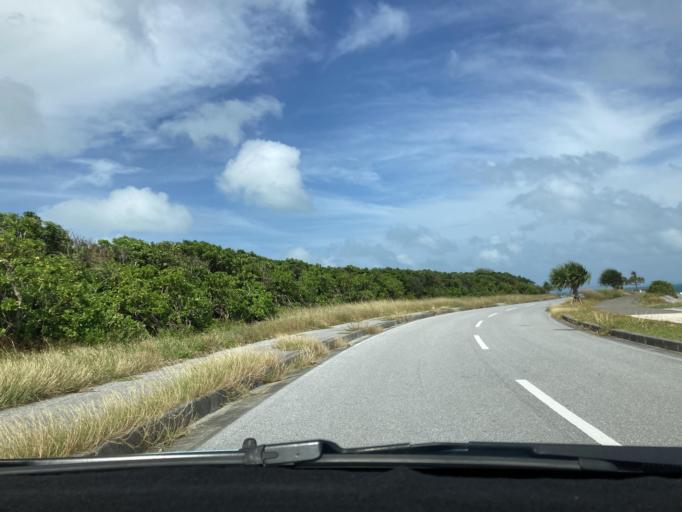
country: JP
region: Okinawa
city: Ginowan
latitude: 26.1829
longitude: 127.8210
